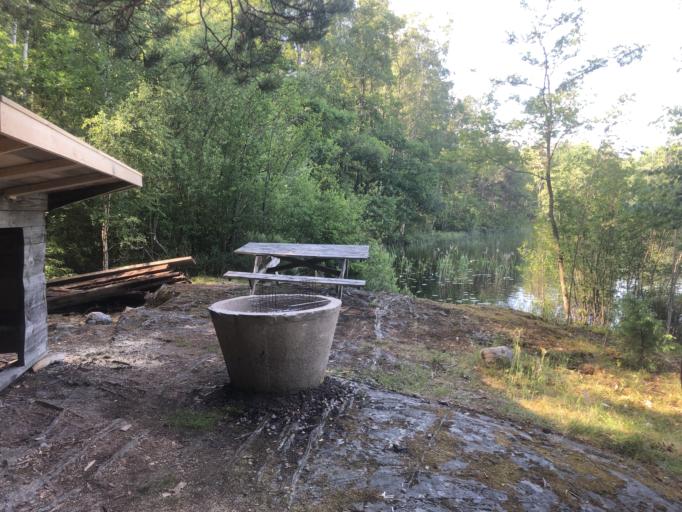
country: SE
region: Kalmar
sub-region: Hogsby Kommun
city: Hoegsby
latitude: 57.3856
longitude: 16.1205
